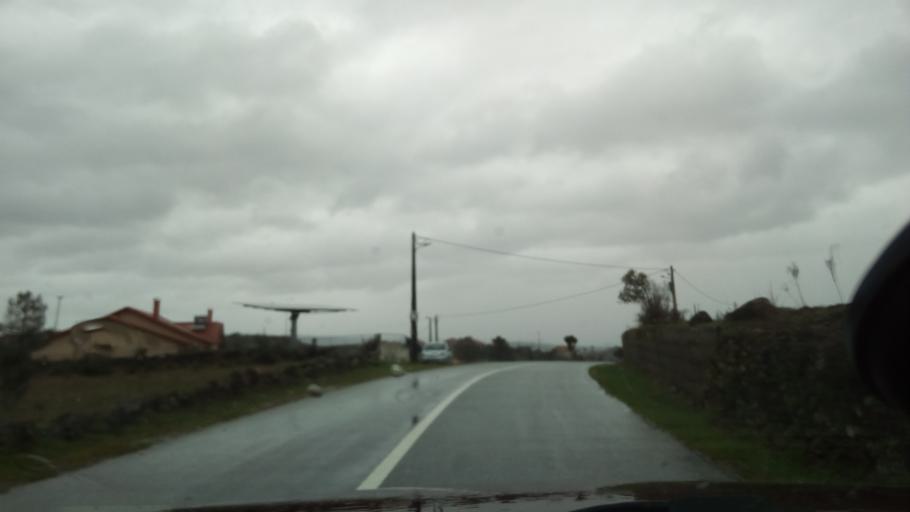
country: PT
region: Guarda
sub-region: Fornos de Algodres
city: Fornos de Algodres
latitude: 40.5641
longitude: -7.5164
